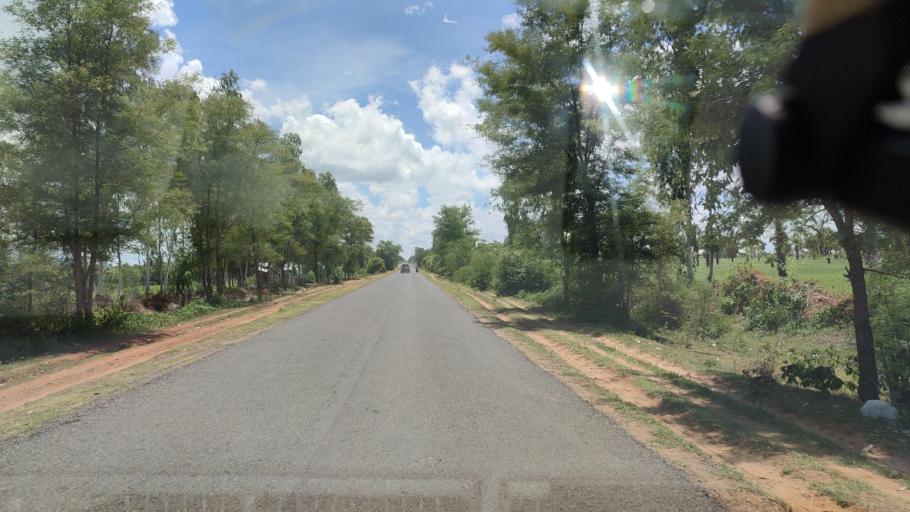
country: MM
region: Magway
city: Magway
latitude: 20.1905
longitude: 95.1833
